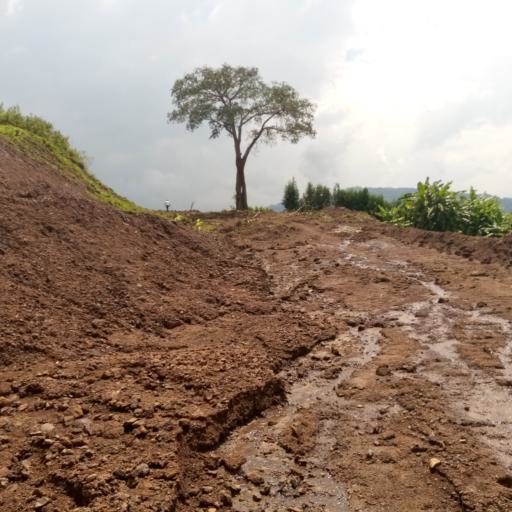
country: ET
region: Southern Nations, Nationalities, and People's Region
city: Arba Minch'
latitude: 6.3164
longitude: 37.3585
